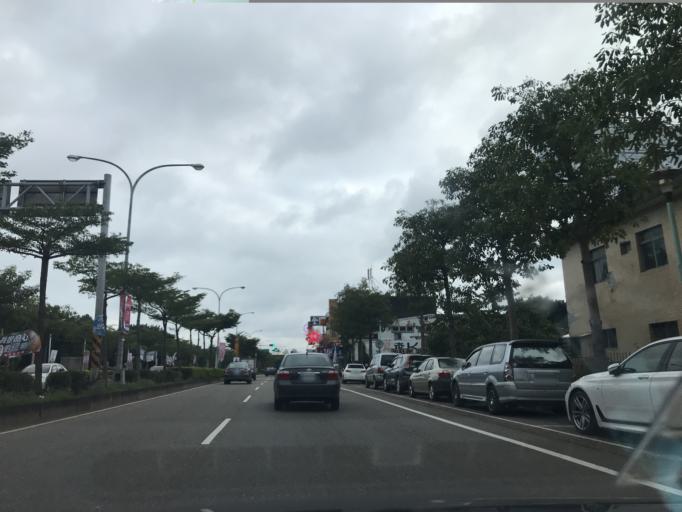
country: TW
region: Taiwan
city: Daxi
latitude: 24.9398
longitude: 121.2162
